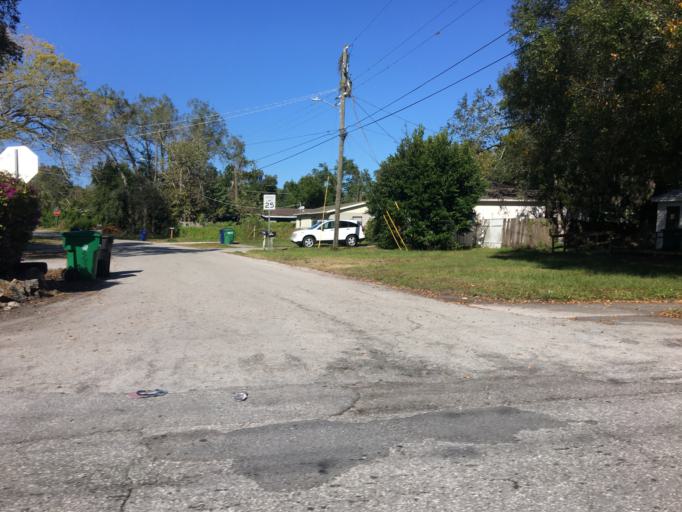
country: US
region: Florida
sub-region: Hillsborough County
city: University
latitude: 28.0399
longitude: -82.4369
